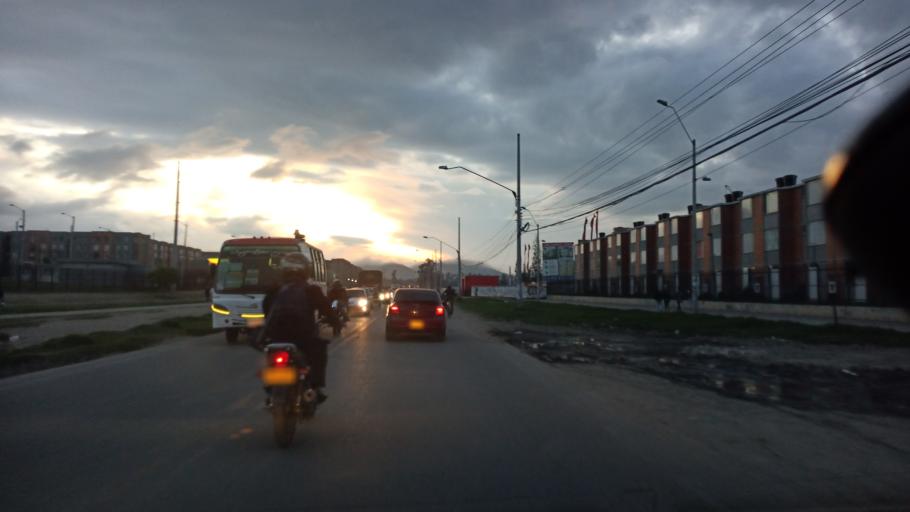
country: CO
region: Cundinamarca
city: Soacha
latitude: 4.5824
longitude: -74.2280
